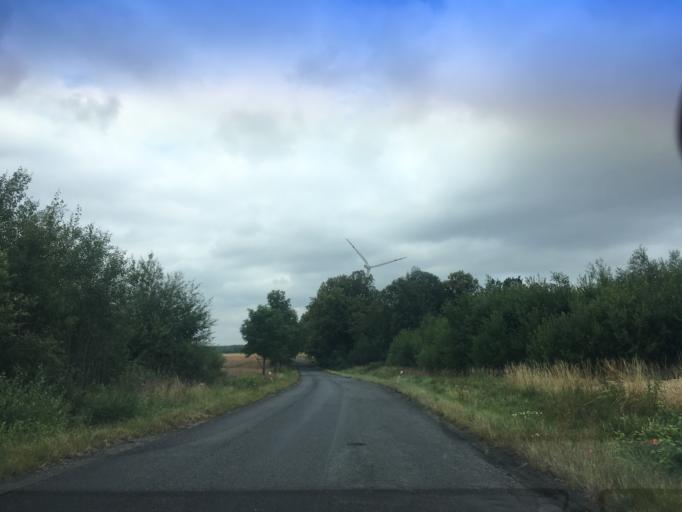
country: PL
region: Lower Silesian Voivodeship
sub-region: Powiat zgorzelecki
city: Sulikow
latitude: 51.0773
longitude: 15.0472
